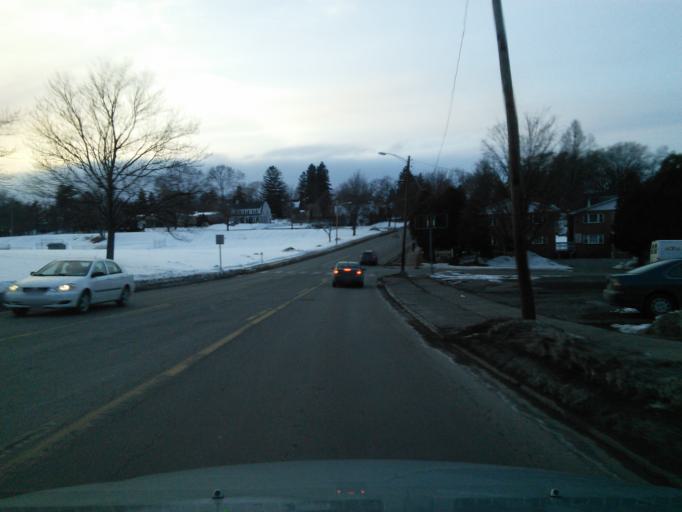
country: US
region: Pennsylvania
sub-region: Centre County
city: State College
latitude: 40.7864
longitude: -77.8575
